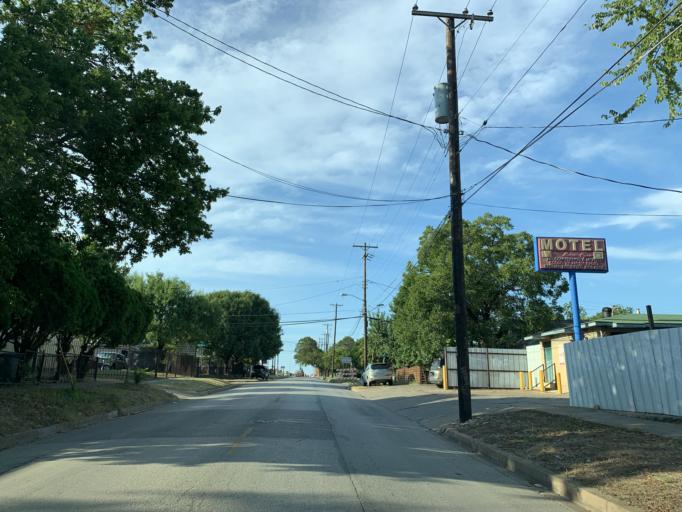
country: US
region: Texas
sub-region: Dallas County
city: Dallas
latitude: 32.7357
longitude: -96.8228
